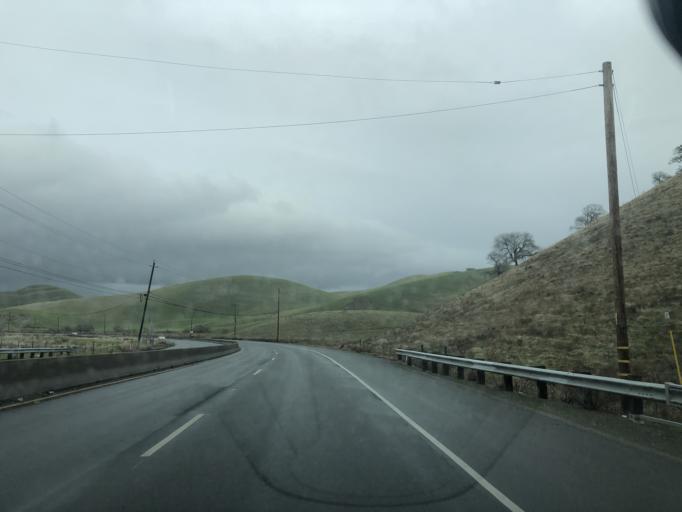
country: US
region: California
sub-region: Contra Costa County
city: Clayton
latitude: 37.9783
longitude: -121.9027
